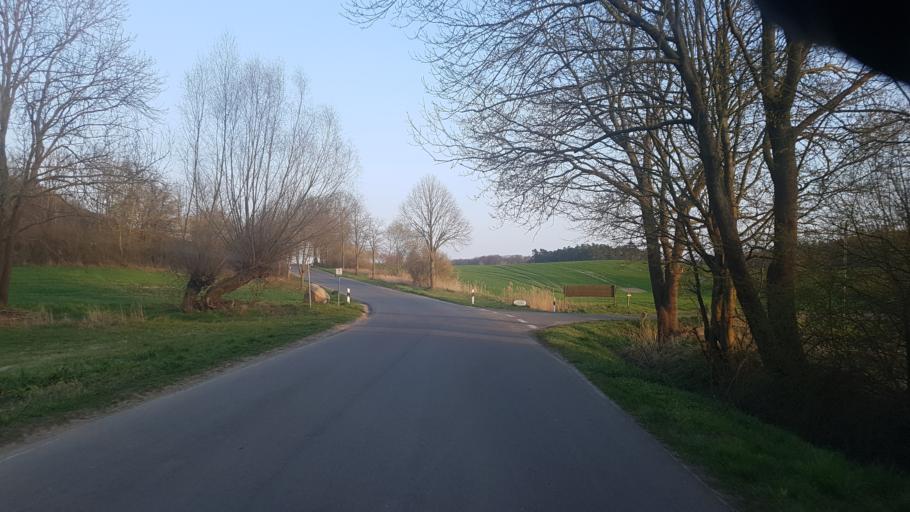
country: DE
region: Brandenburg
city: Gramzow
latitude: 53.2143
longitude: 13.9396
